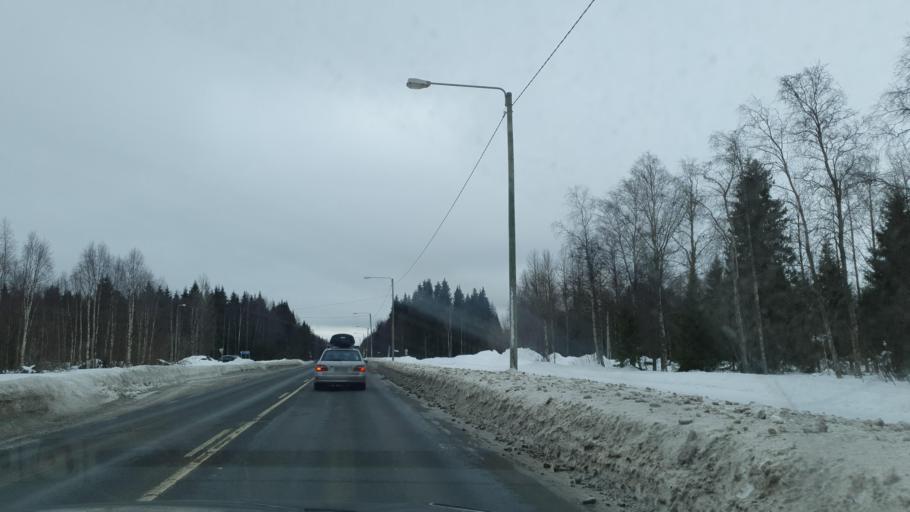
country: FI
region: Lapland
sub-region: Kemi-Tornio
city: Tornio
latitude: 66.0195
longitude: 24.0535
